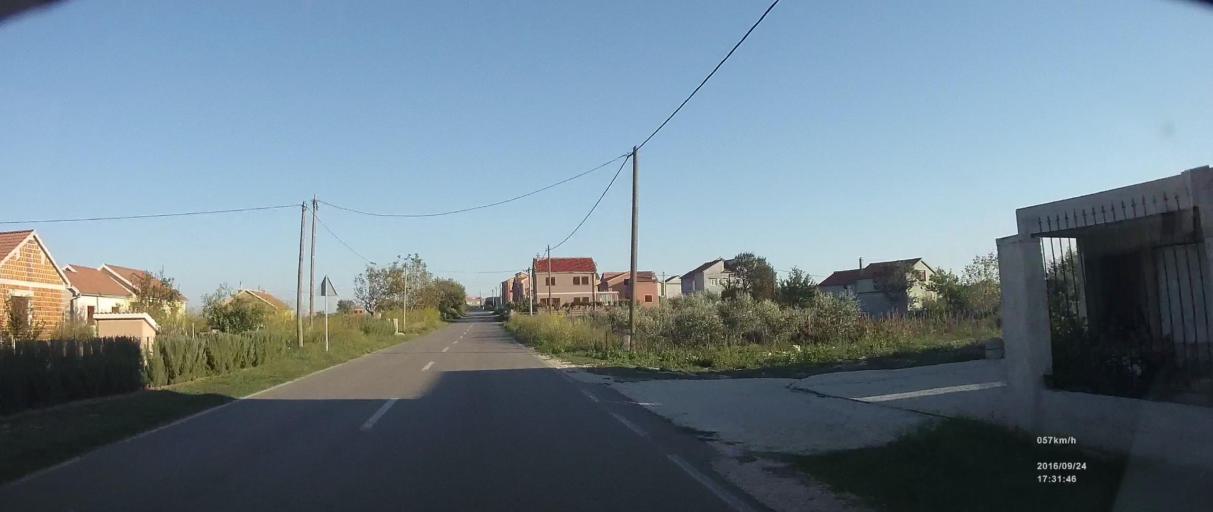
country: HR
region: Zadarska
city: Posedarje
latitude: 44.1867
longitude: 15.4450
